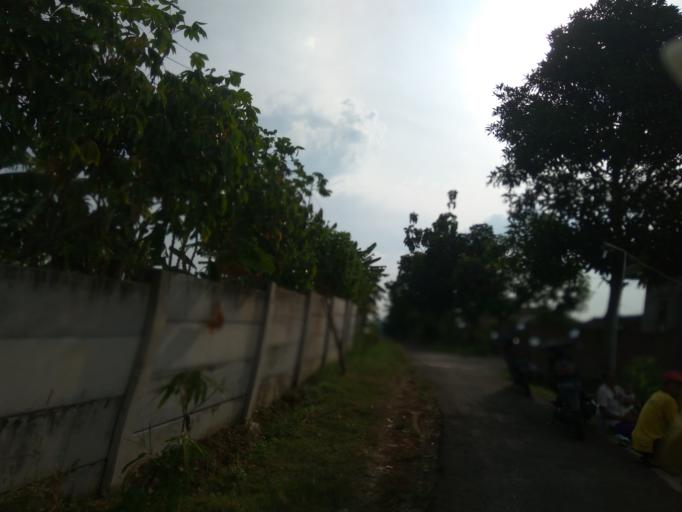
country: ID
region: Central Java
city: Semarang
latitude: -7.0210
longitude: 110.4462
